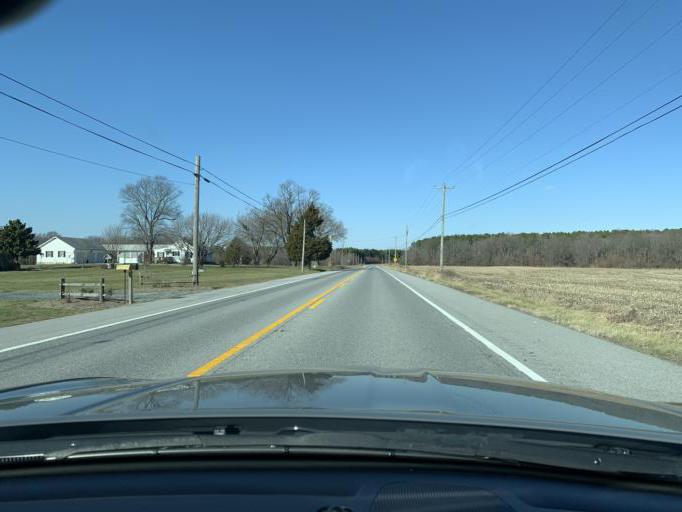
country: US
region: Maryland
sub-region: Queen Anne's County
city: Centreville
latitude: 39.0903
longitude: -76.0335
